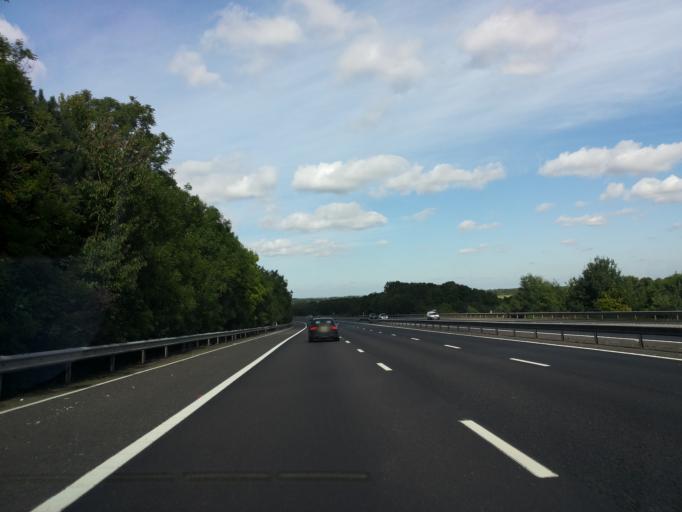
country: GB
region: England
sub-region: Kent
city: Kemsing
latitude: 51.3385
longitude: 0.2746
